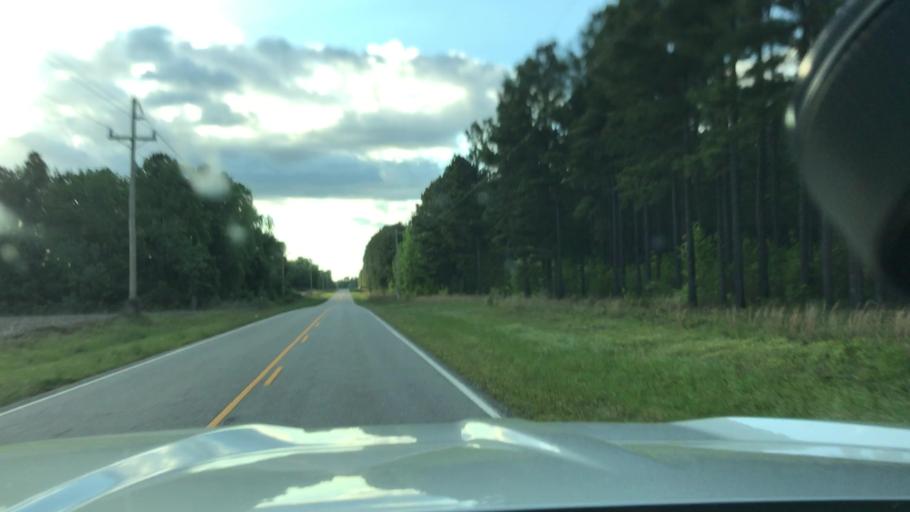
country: US
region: South Carolina
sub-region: Bamberg County
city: Denmark
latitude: 33.4665
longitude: -81.1613
